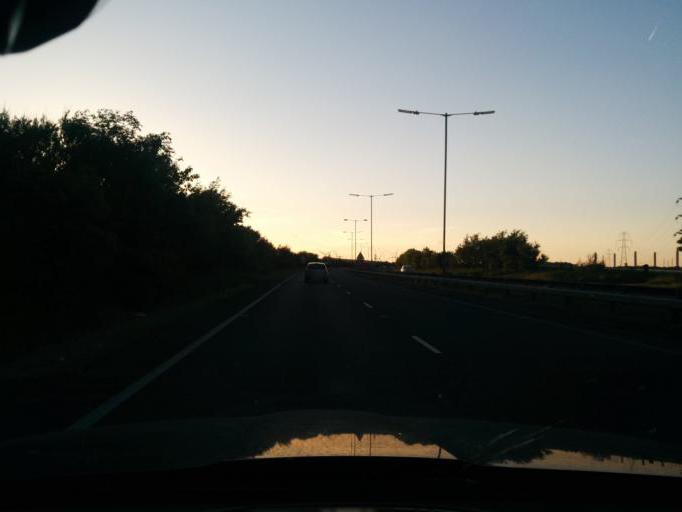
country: GB
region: England
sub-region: Northumberland
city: Newbiggin-by-the-Sea
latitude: 55.1822
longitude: -1.5357
